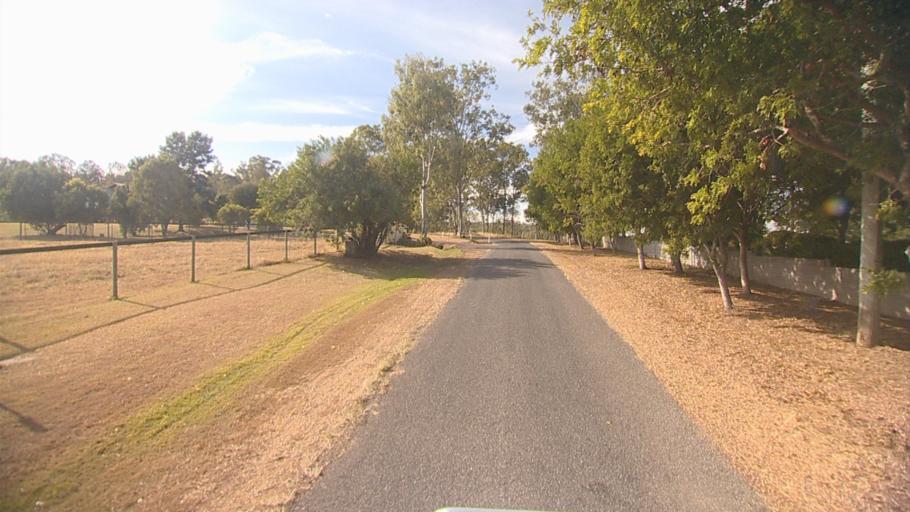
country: AU
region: Queensland
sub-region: Logan
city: Cedar Vale
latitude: -27.9089
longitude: 152.9849
